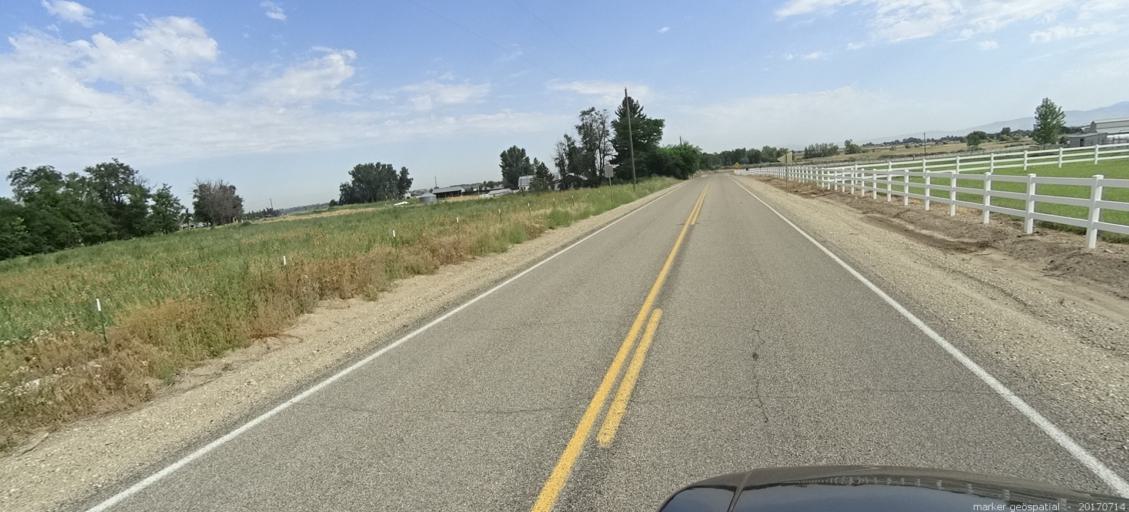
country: US
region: Idaho
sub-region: Ada County
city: Kuna
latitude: 43.5001
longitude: -116.3543
